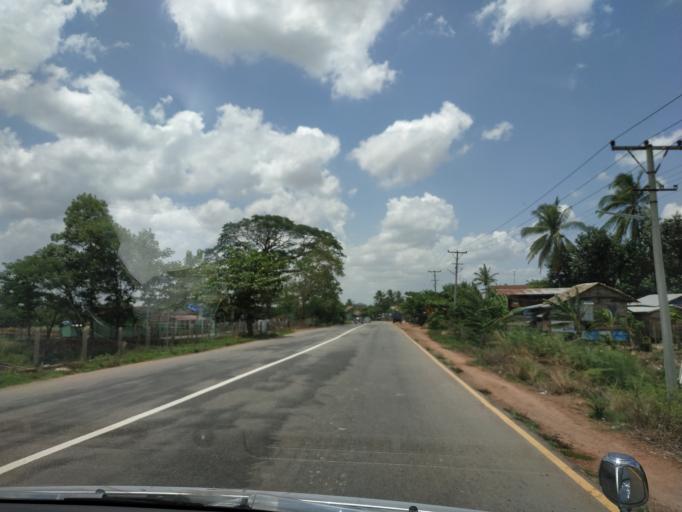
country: MM
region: Bago
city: Thanatpin
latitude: 17.5098
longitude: 96.7151
